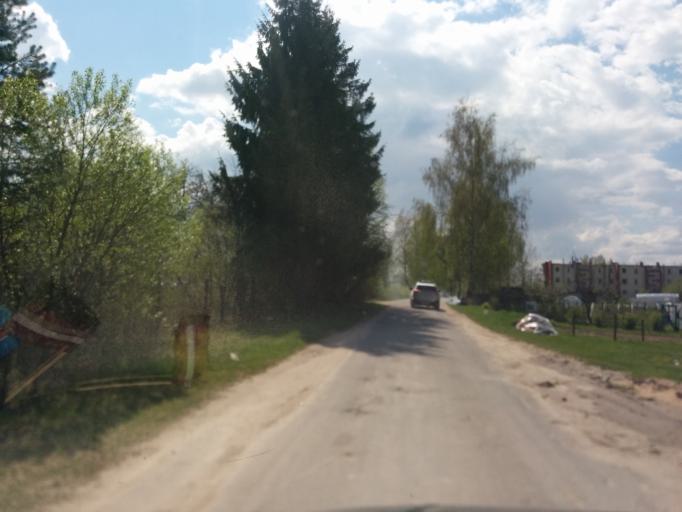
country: LV
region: Ozolnieku
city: Ozolnieki
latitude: 56.6352
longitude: 23.7904
